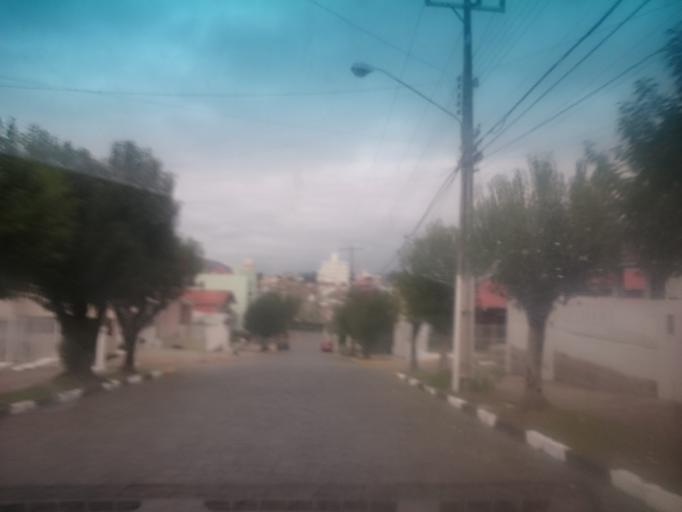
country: BR
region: Santa Catarina
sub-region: Lages
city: Lages
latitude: -27.8181
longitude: -50.3219
